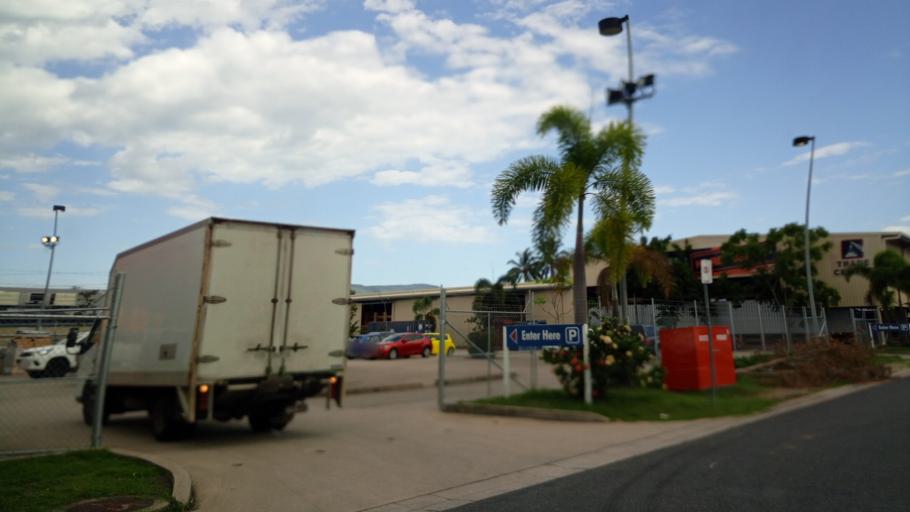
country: AU
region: Queensland
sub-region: Cairns
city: Woree
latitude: -16.9362
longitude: 145.7547
